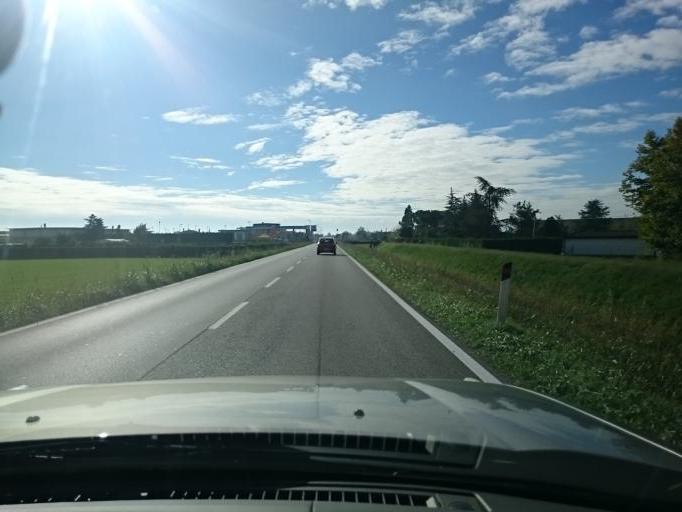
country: IT
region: Veneto
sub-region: Provincia di Padova
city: Bovolenta
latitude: 45.2825
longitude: 11.9288
